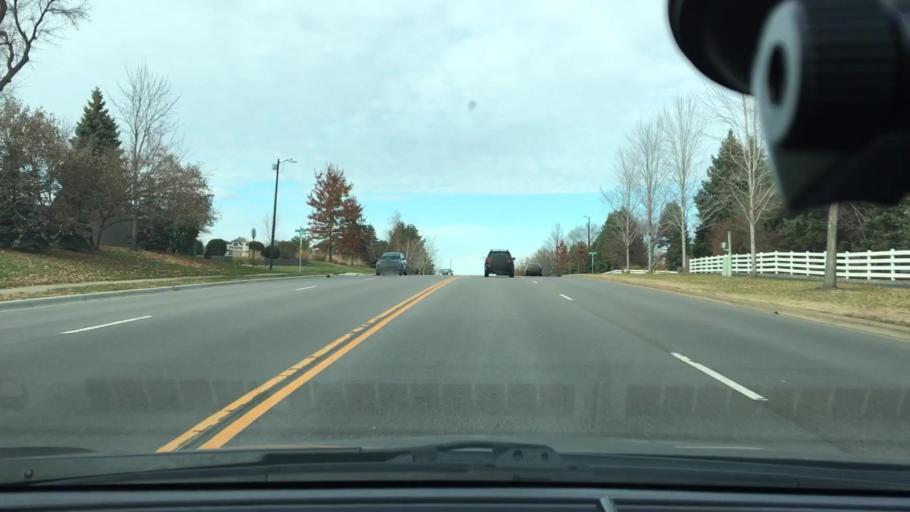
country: US
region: Minnesota
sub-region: Hennepin County
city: Maple Grove
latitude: 45.1124
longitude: -93.4922
